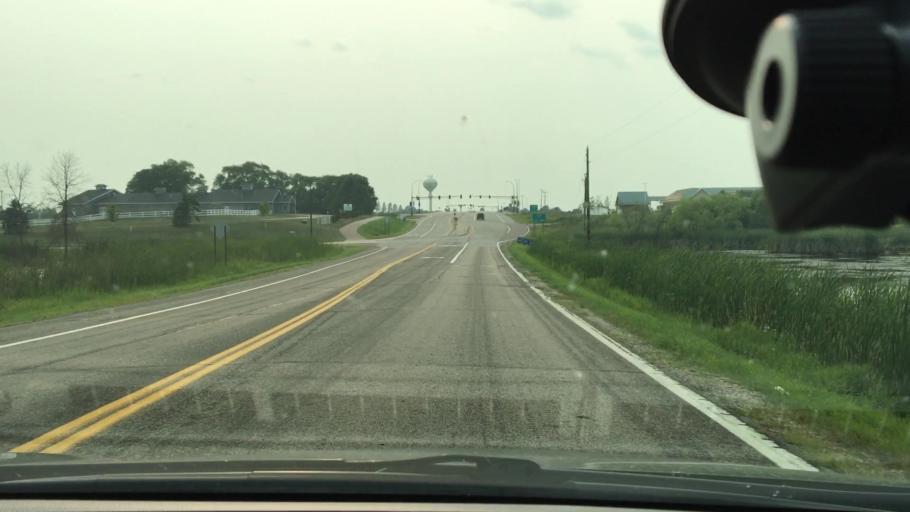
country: US
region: Minnesota
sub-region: Hennepin County
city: Dayton
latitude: 45.2524
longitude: -93.5491
